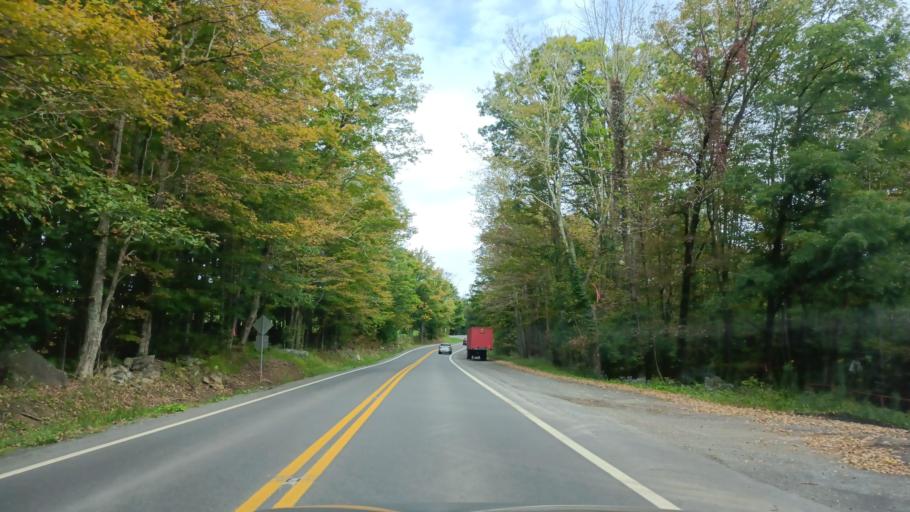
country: US
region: Maryland
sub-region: Garrett County
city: Mountain Lake Park
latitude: 39.2827
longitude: -79.3192
